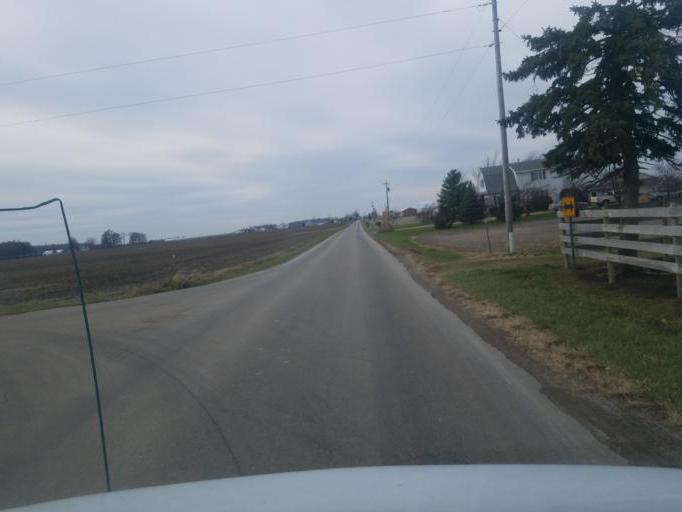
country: US
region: Indiana
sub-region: Adams County
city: Geneva
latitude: 40.6152
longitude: -84.8588
